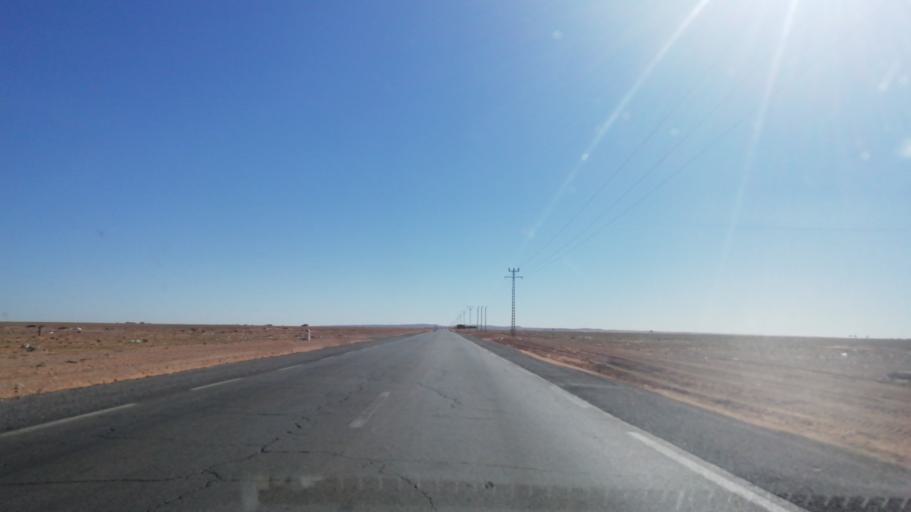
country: DZ
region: Saida
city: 'Ain el Hadjar
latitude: 34.0178
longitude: 0.1080
